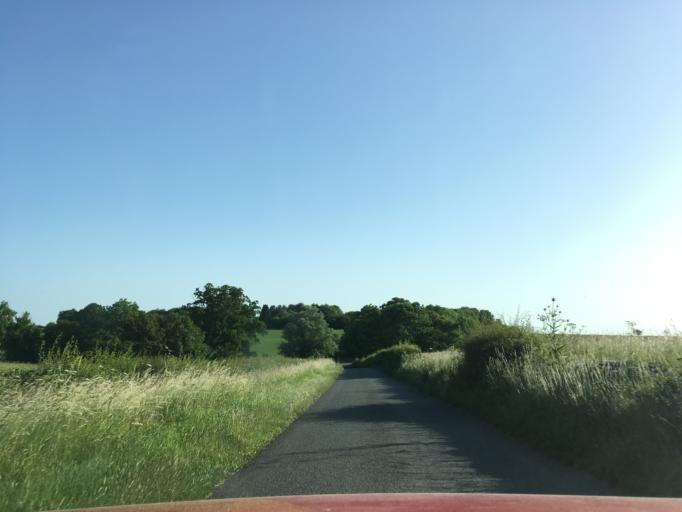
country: GB
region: England
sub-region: Gloucestershire
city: Fairford
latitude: 51.7381
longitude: -1.7361
